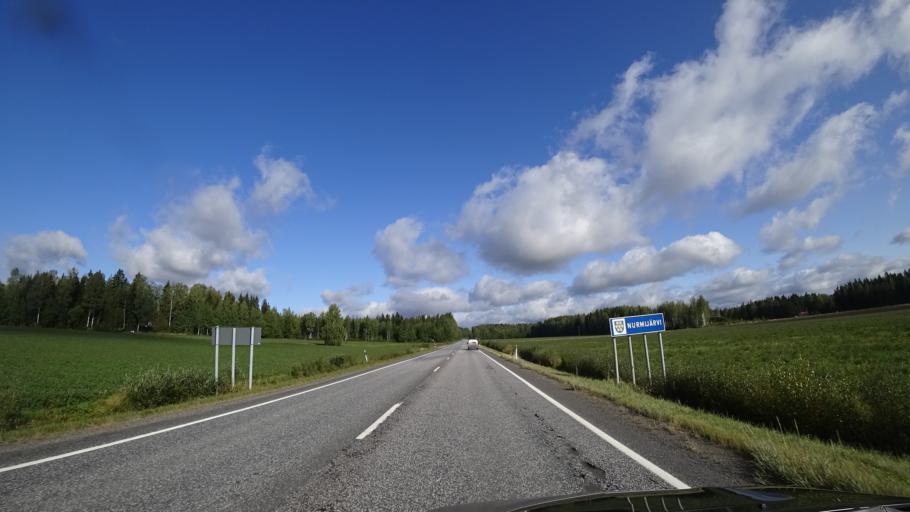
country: FI
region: Uusimaa
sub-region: Helsinki
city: Tuusula
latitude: 60.4694
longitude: 24.9439
